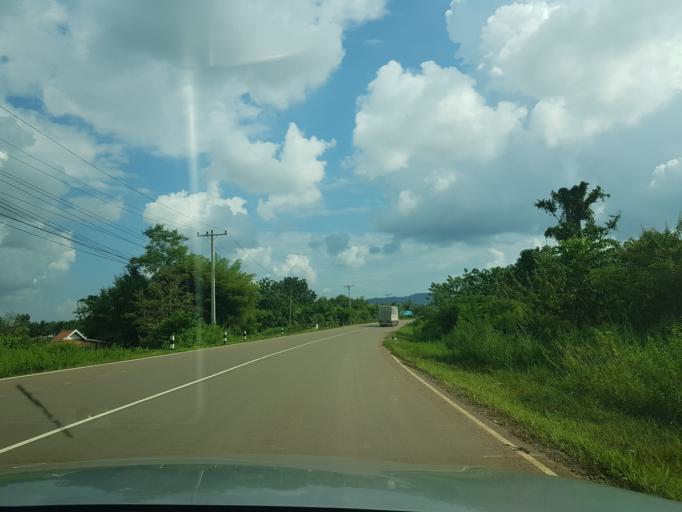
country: TH
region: Nong Khai
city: Sangkhom
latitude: 18.0851
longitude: 102.2925
